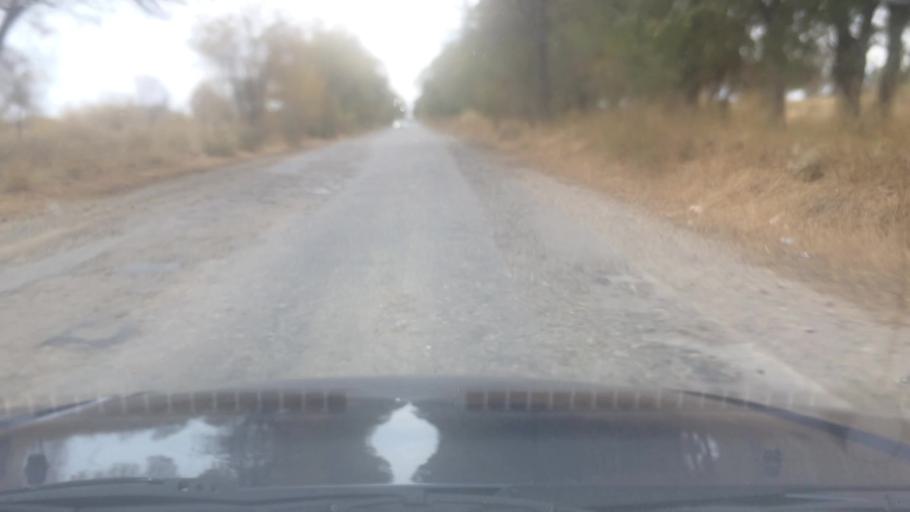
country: KG
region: Ysyk-Koel
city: Balykchy
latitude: 42.3049
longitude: 76.4738
